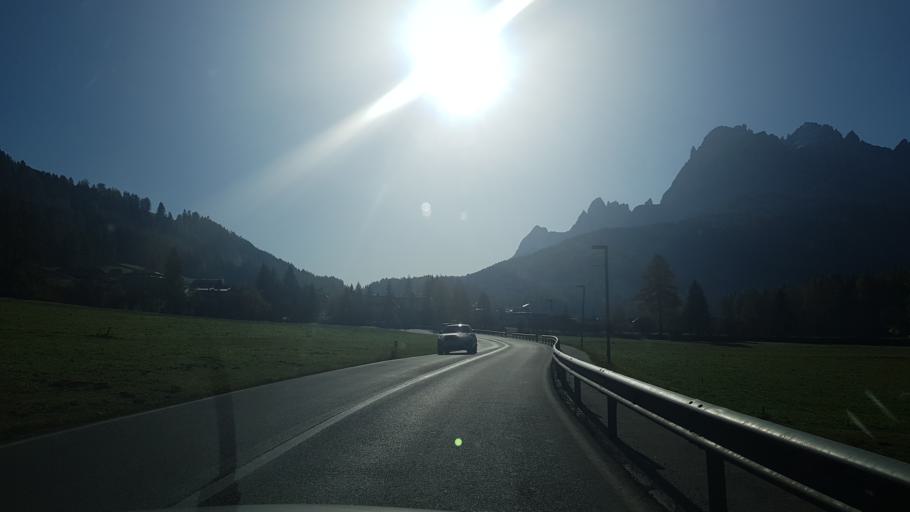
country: IT
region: Trentino-Alto Adige
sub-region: Bolzano
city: Sesto
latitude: 46.6943
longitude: 12.3612
